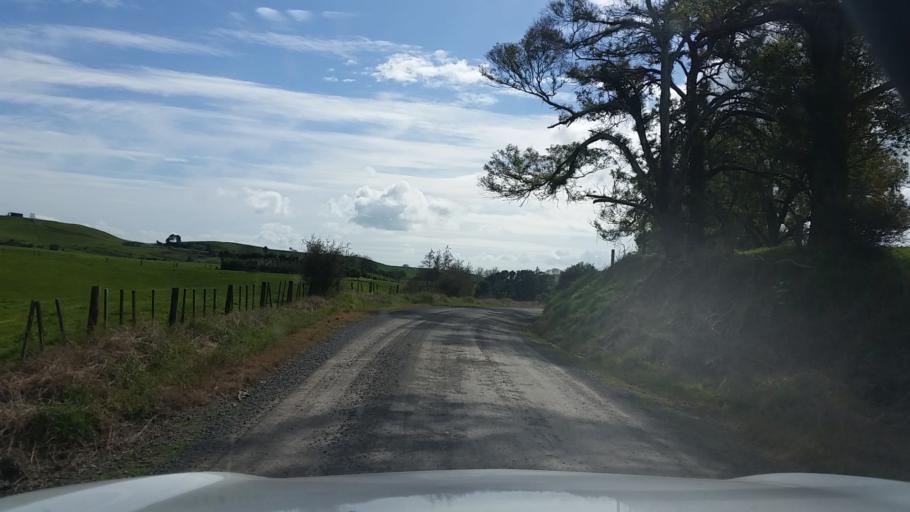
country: NZ
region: Waikato
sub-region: Hauraki District
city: Ngatea
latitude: -37.4534
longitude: 175.5006
